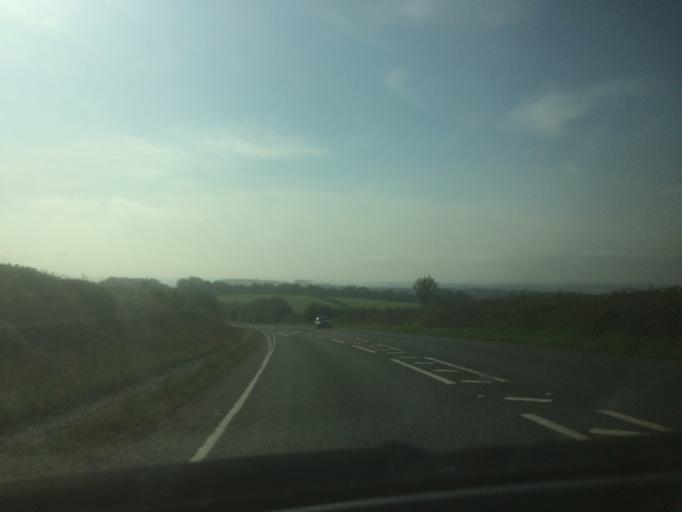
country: GB
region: England
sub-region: Cornwall
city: Pillaton
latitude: 50.4781
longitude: -4.2839
